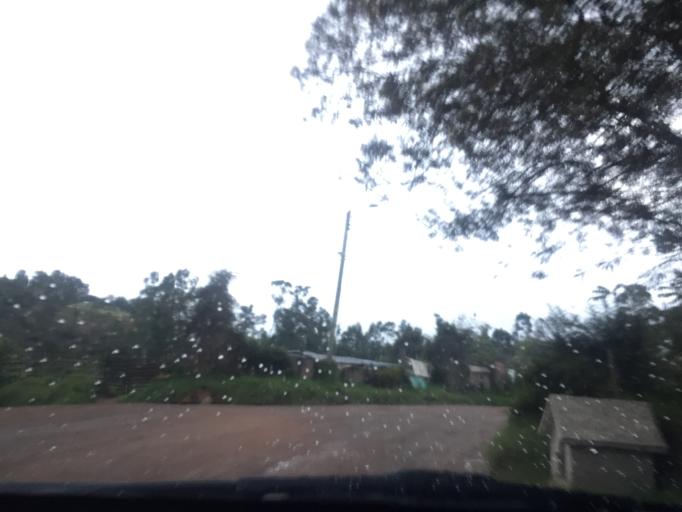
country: CO
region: Cundinamarca
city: Cogua
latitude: 5.0665
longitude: -73.9504
